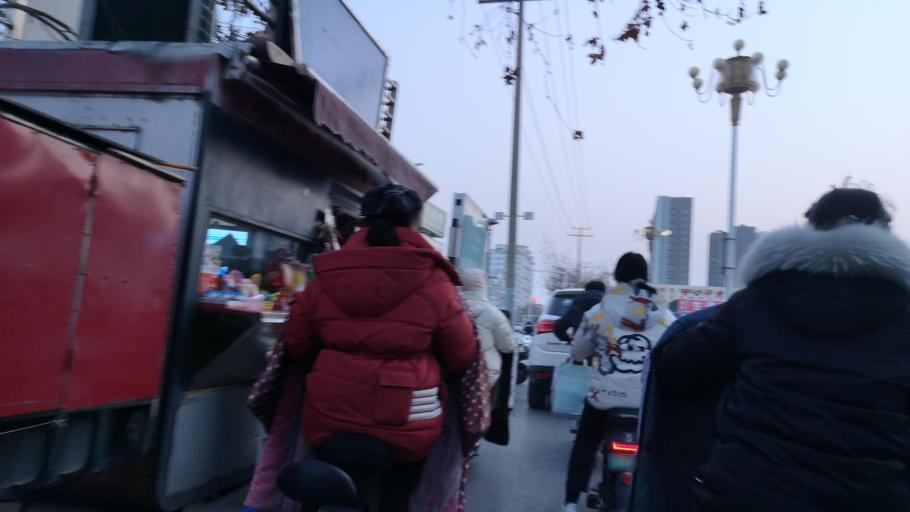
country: CN
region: Henan Sheng
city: Zhongyuanlu
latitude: 35.7713
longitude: 115.0695
